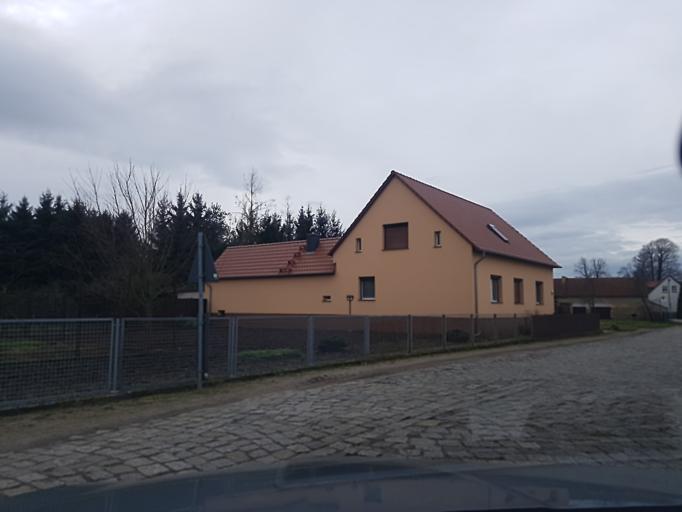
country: DE
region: Brandenburg
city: Schilda
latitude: 51.5899
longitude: 13.3849
